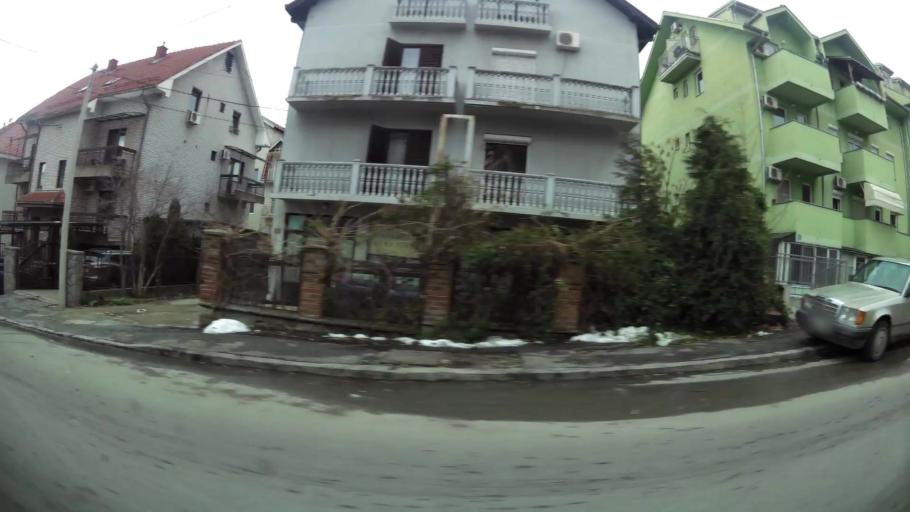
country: RS
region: Central Serbia
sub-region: Belgrade
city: Cukarica
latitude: 44.7545
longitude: 20.4081
